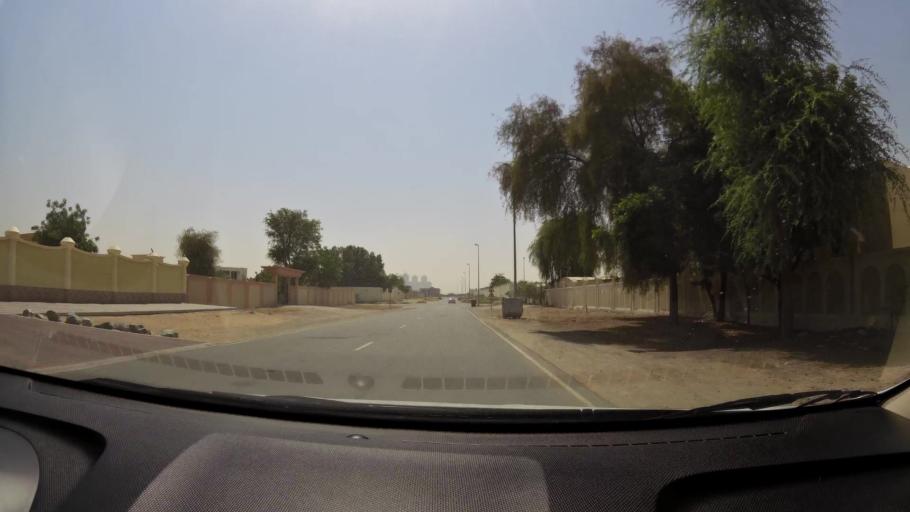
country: AE
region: Ajman
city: Ajman
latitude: 25.3938
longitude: 55.5389
